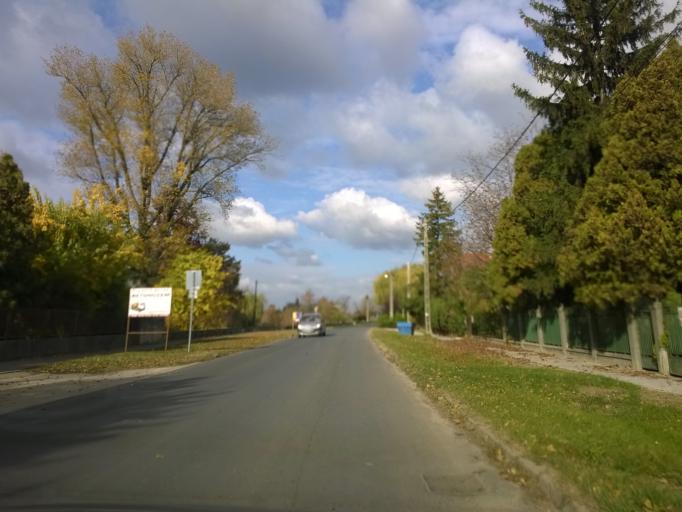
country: HU
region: Pest
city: Rackeve
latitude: 47.1603
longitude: 18.9518
